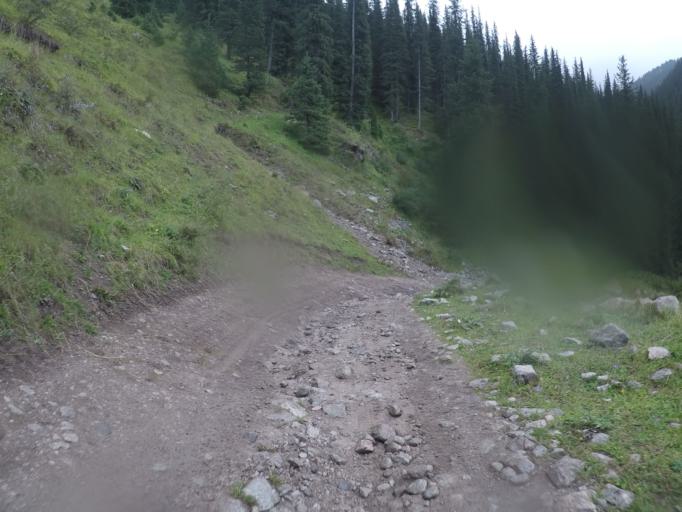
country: KG
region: Ysyk-Koel
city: Teploklyuchenka
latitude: 42.4106
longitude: 78.5780
